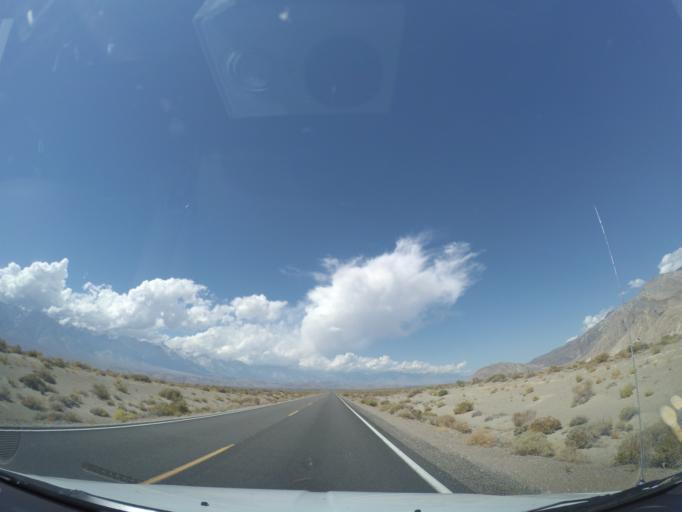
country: US
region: California
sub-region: Inyo County
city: Lone Pine
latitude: 36.5562
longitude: -117.9606
